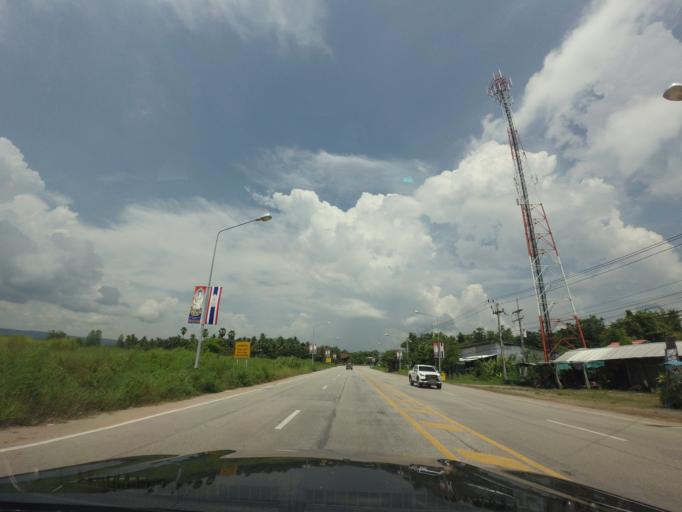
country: TH
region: Khon Kaen
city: Wiang Kao
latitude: 16.6728
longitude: 102.2978
